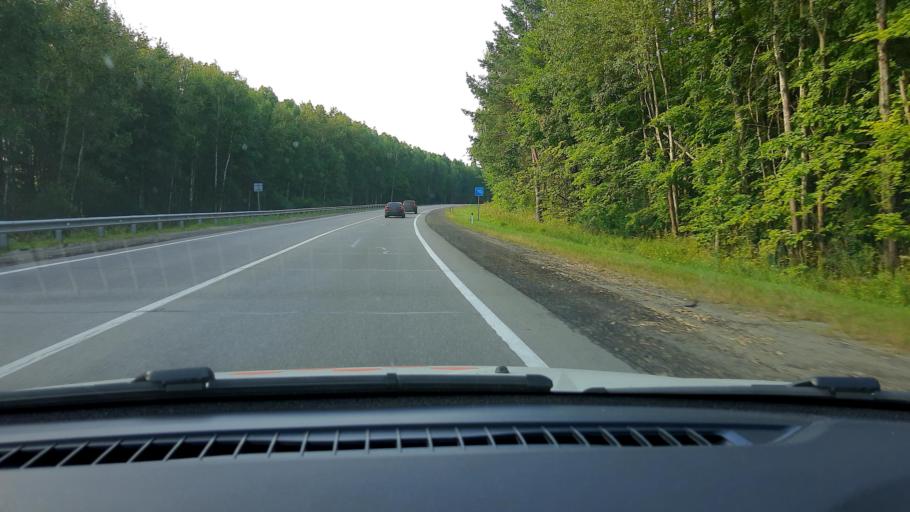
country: RU
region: Nizjnij Novgorod
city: Surovatikha
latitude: 55.5960
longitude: 43.9859
